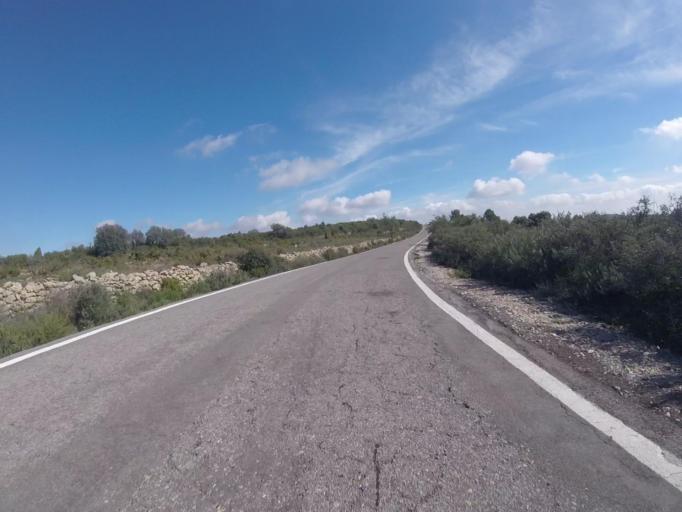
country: ES
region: Valencia
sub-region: Provincia de Castello
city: Sarratella
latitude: 40.3304
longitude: 0.0323
